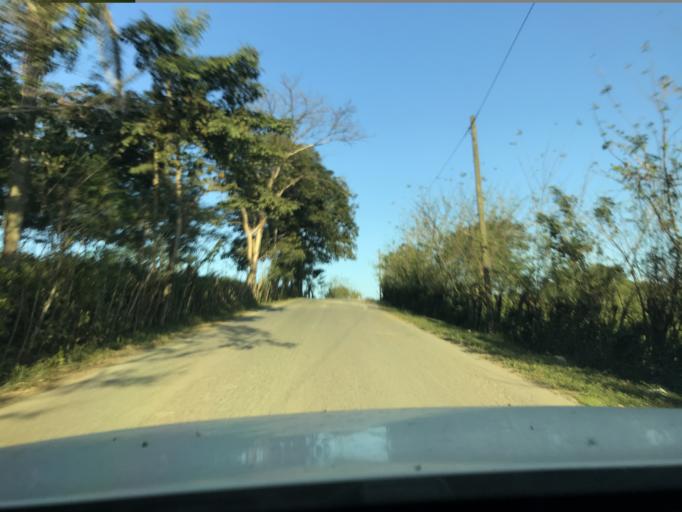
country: GT
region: Izabal
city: Morales
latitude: 15.6398
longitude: -89.0364
